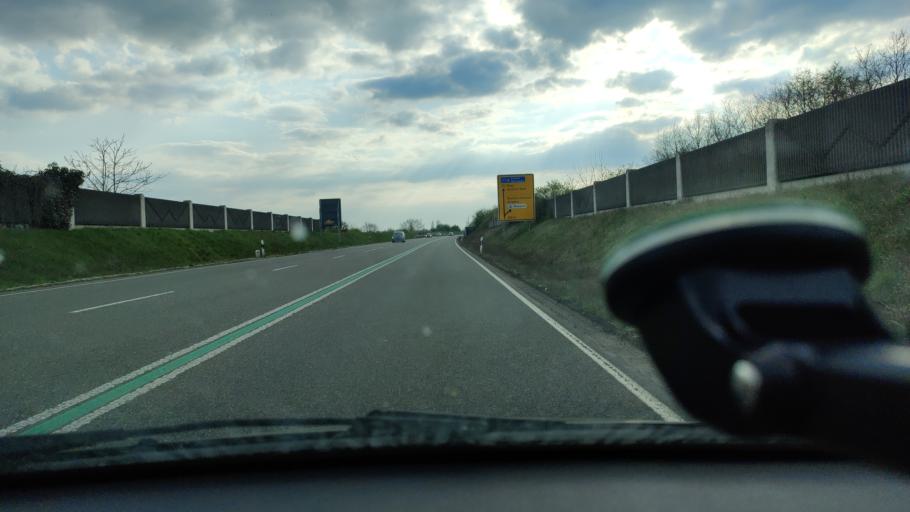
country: DE
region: North Rhine-Westphalia
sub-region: Regierungsbezirk Dusseldorf
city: Bocholt
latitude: 51.8210
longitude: 6.6220
